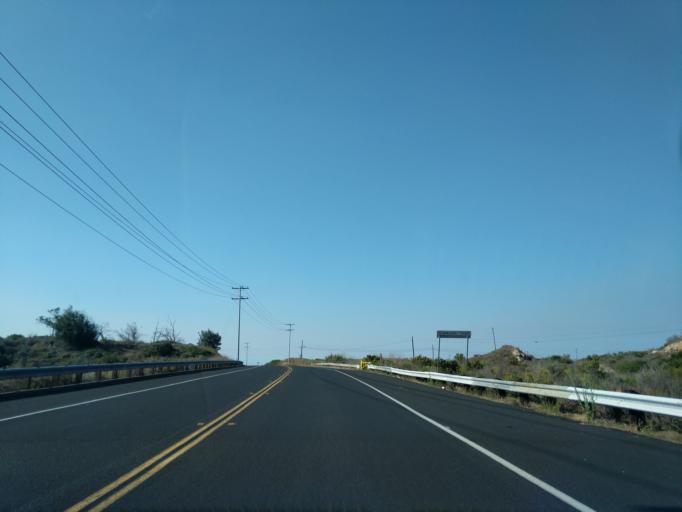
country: US
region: California
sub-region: Orange County
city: San Clemente
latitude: 33.4039
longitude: -117.5885
